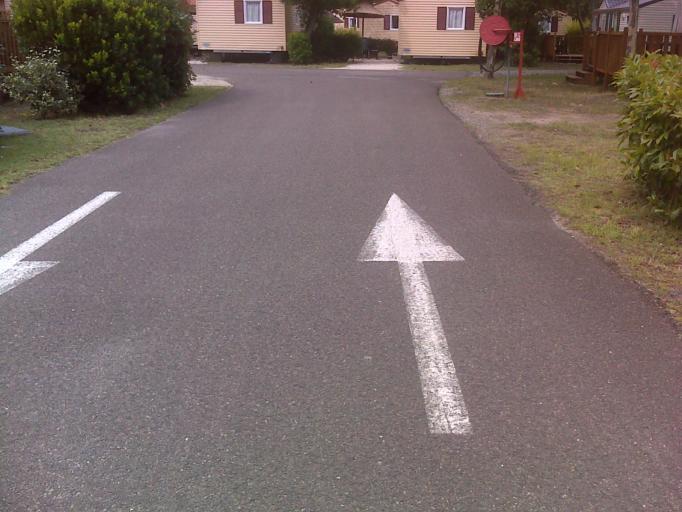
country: FR
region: Aquitaine
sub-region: Departement des Landes
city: Biscarrosse
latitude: 44.4377
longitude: -1.1578
